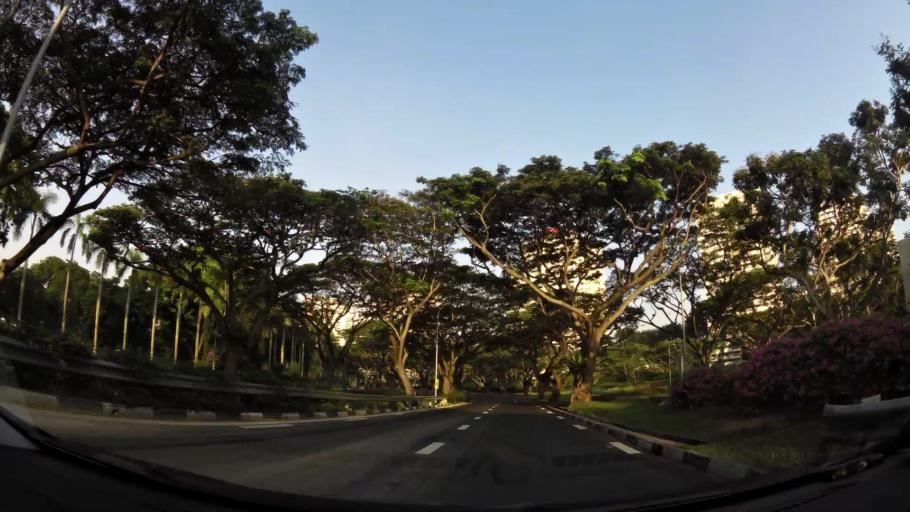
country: SG
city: Singapore
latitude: 1.3077
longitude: 103.9342
